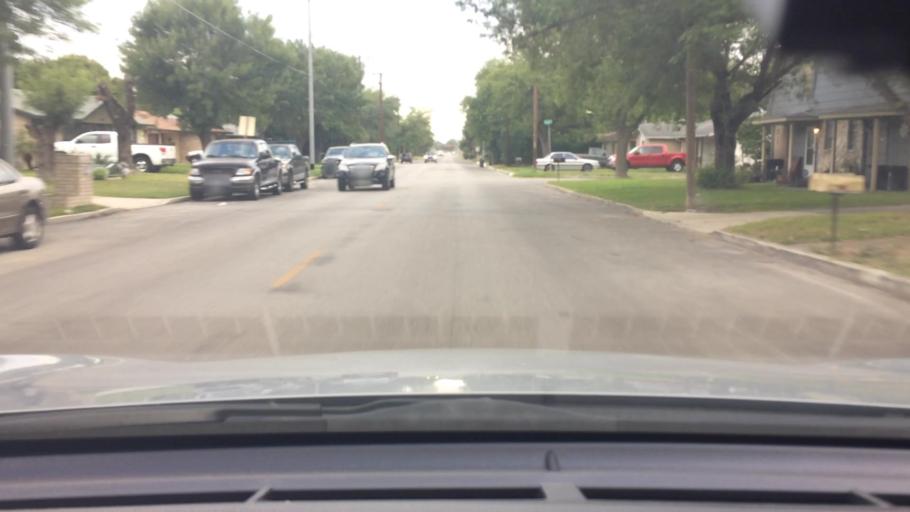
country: US
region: Texas
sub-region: Bexar County
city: Universal City
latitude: 29.5443
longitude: -98.2953
